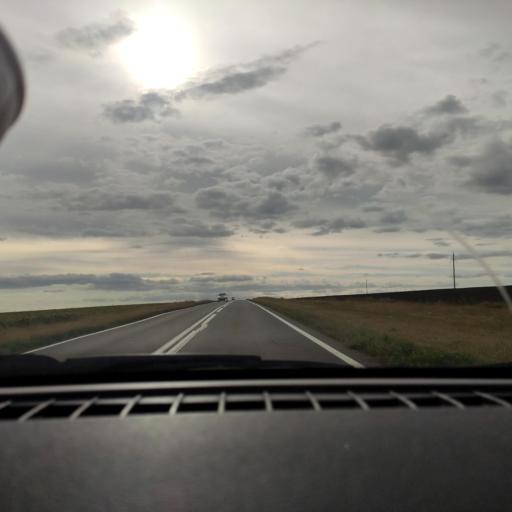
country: RU
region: Samara
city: Georgiyevka
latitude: 53.4169
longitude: 50.8998
